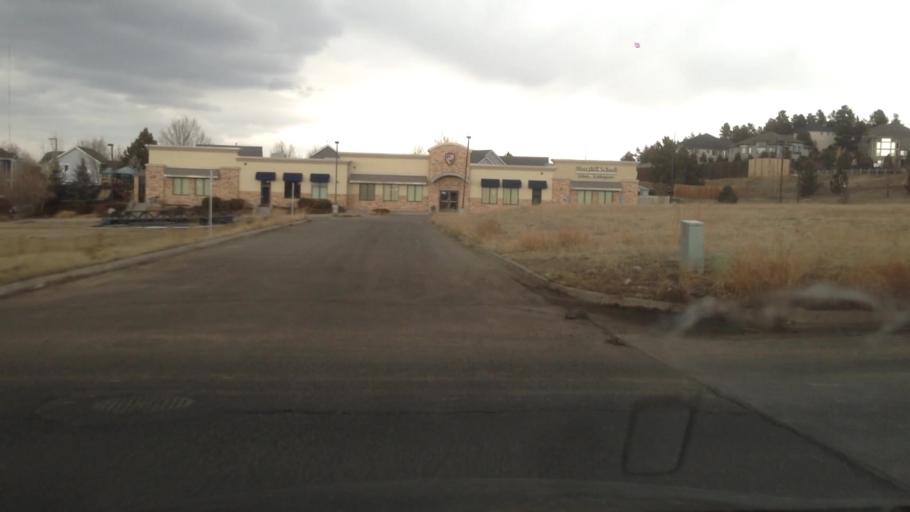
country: US
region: Colorado
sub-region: Douglas County
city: Parker
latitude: 39.4938
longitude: -104.7616
